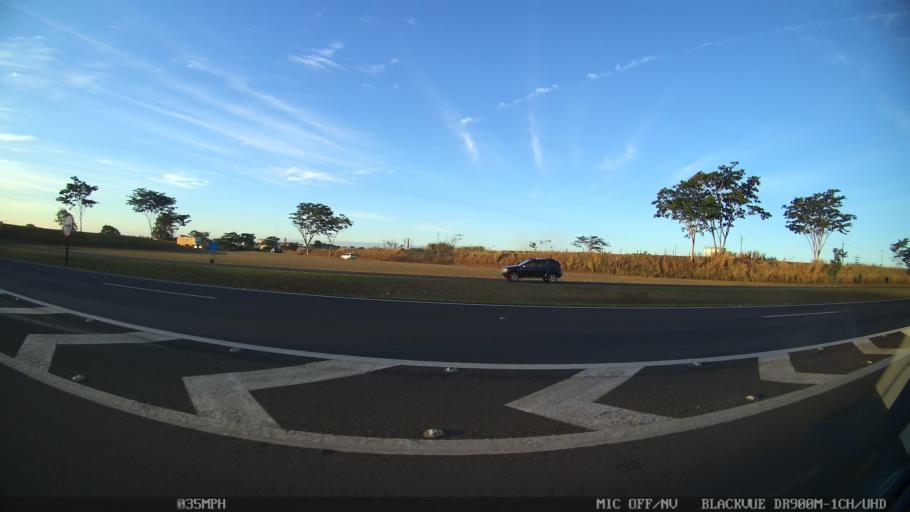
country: BR
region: Sao Paulo
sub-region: Catanduva
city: Catanduva
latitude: -21.1355
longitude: -49.0184
